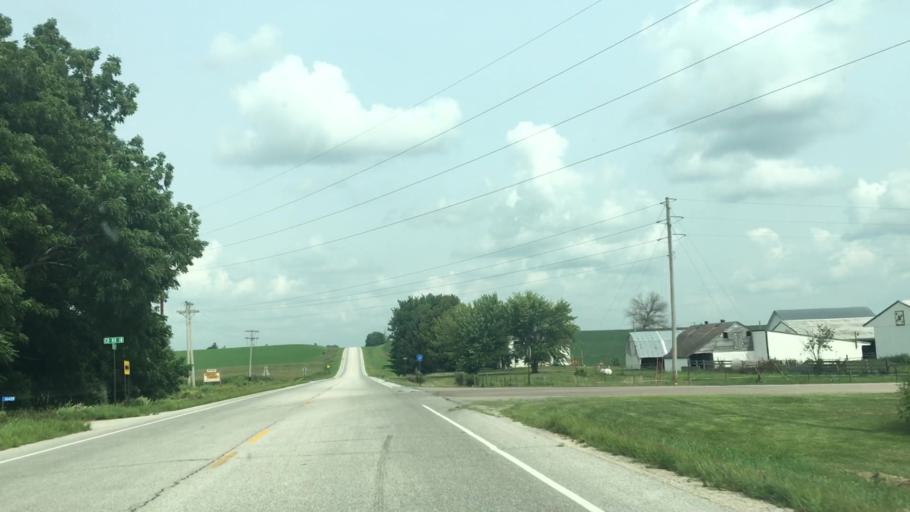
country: US
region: Minnesota
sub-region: Fillmore County
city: Harmony
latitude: 43.5943
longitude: -91.9297
